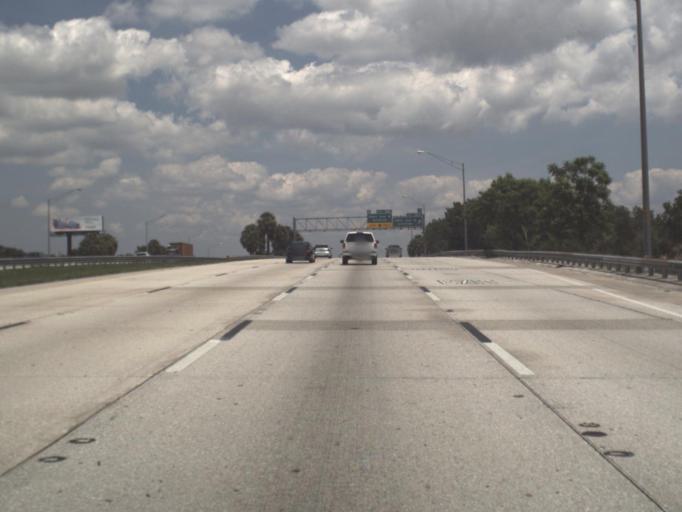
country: US
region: Florida
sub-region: Pinellas County
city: Lealman
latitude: 27.8154
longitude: -82.6645
